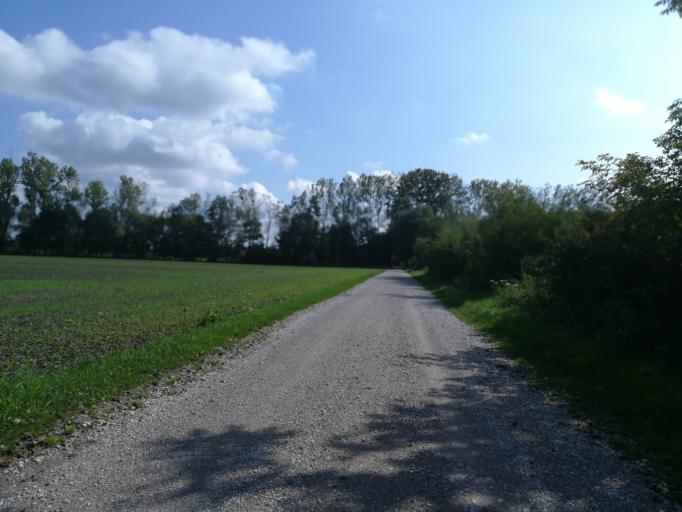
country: DE
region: Bavaria
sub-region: Upper Bavaria
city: Karlsfeld
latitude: 48.2275
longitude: 11.5028
